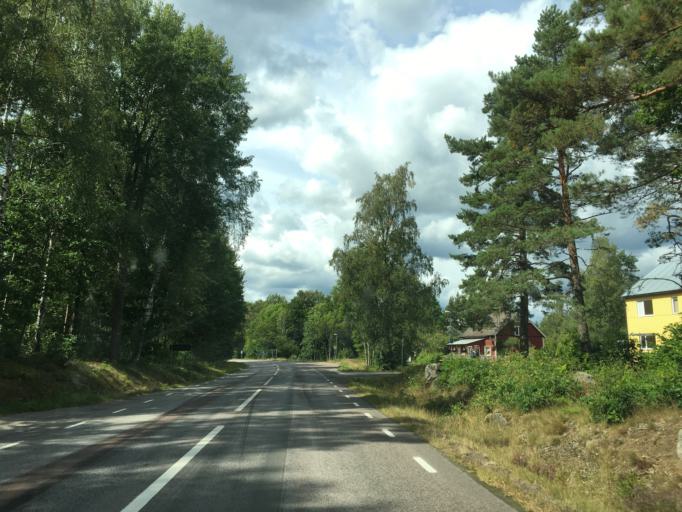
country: SE
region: Kalmar
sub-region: Nybro Kommun
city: Nybro
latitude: 56.9276
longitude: 15.9370
